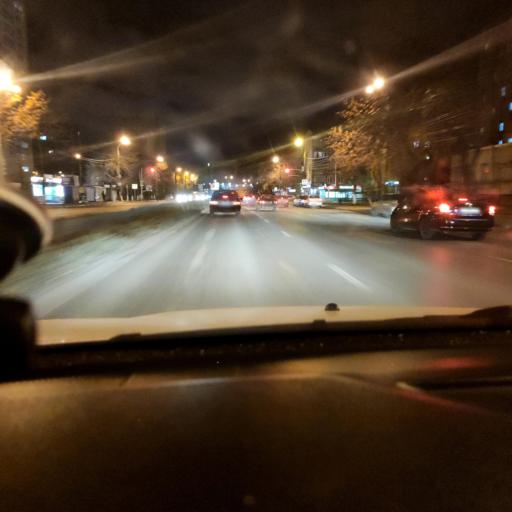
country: RU
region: Samara
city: Samara
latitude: 53.2008
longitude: 50.1676
